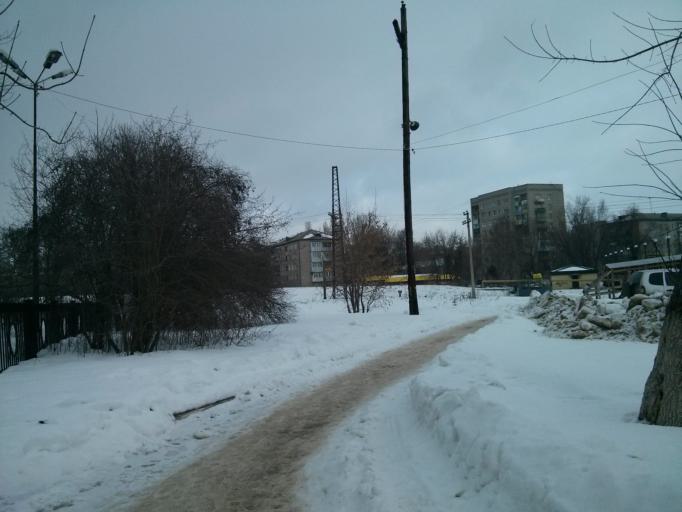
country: RU
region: Vladimir
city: Murom
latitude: 55.5633
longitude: 42.0573
